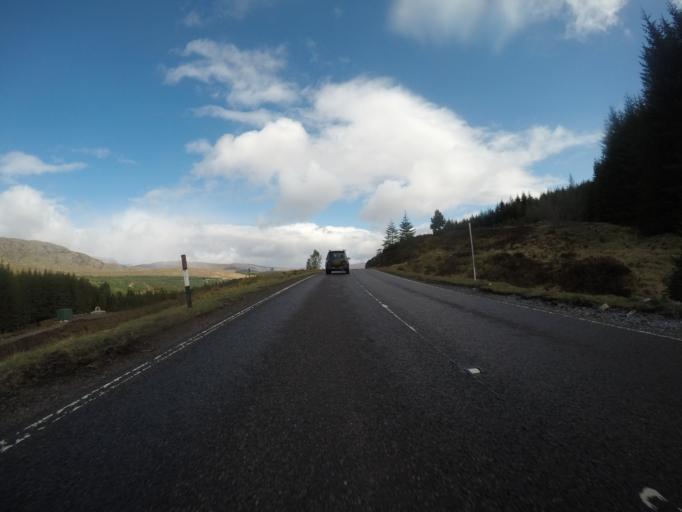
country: GB
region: Scotland
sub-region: Highland
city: Spean Bridge
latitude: 57.1083
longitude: -4.9848
